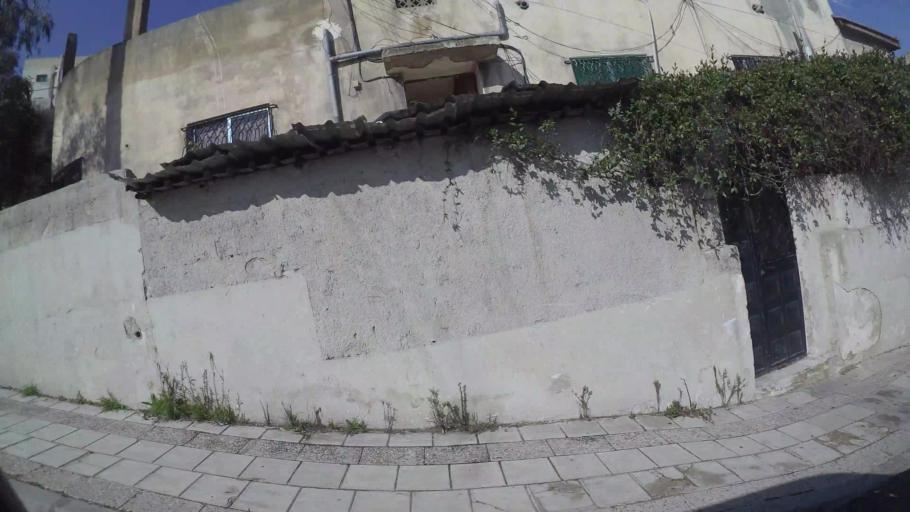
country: JO
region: Amman
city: Amman
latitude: 31.9373
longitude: 35.9093
